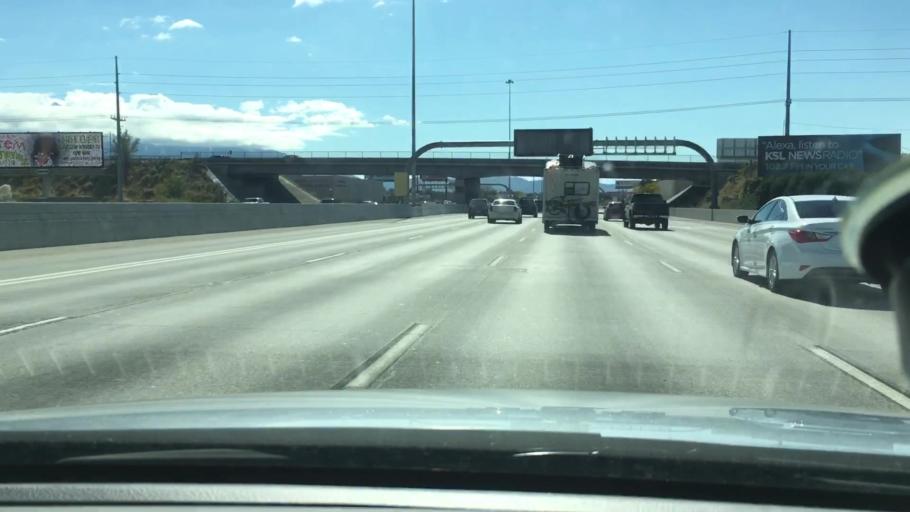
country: US
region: Utah
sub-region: Salt Lake County
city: Centerfield
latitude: 40.6880
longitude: -111.9034
